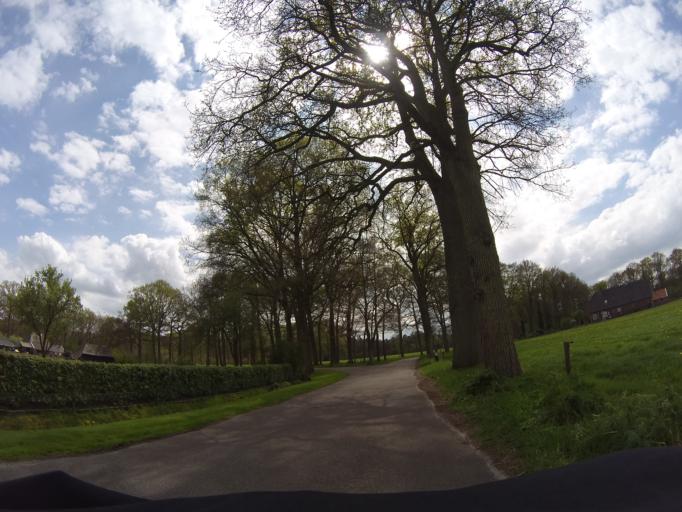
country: NL
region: Overijssel
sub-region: Gemeente Twenterand
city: Den Ham
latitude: 52.5193
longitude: 6.4890
